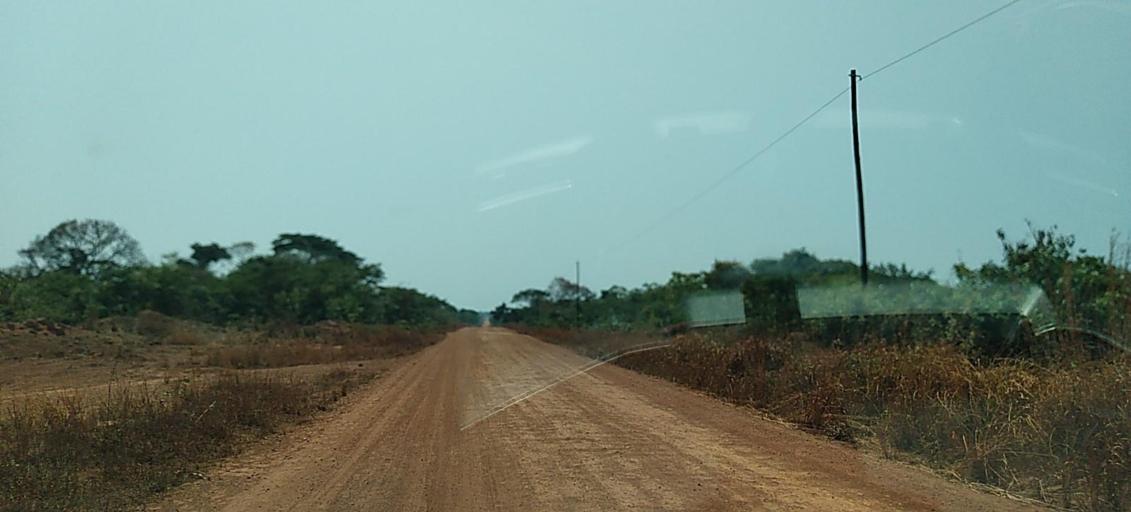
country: ZM
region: North-Western
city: Kansanshi
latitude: -11.9926
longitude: 26.6225
